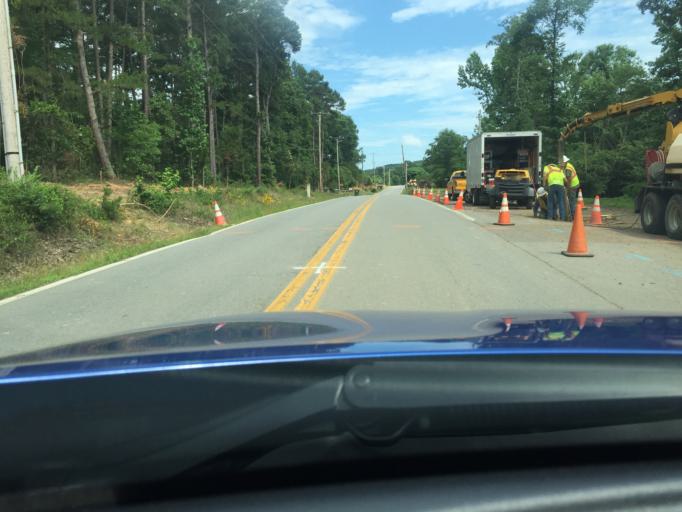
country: US
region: Arkansas
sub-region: Pulaski County
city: Maumelle
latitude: 34.8069
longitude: -92.4384
